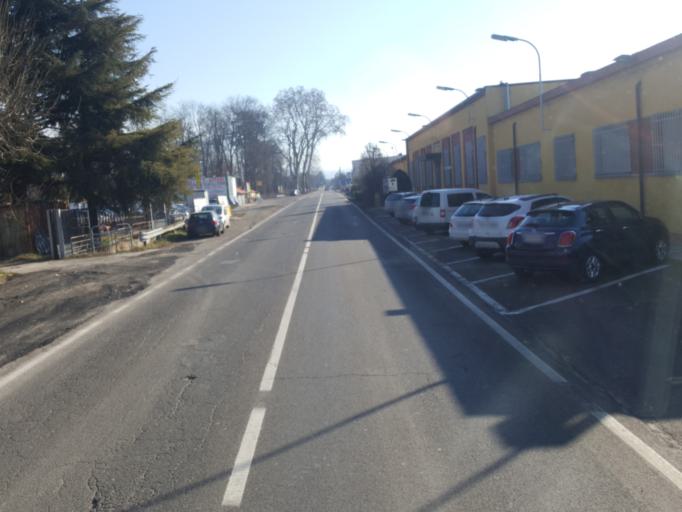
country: IT
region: Piedmont
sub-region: Provincia di Alessandria
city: Castellar Guidobono
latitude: 44.9058
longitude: 8.9410
